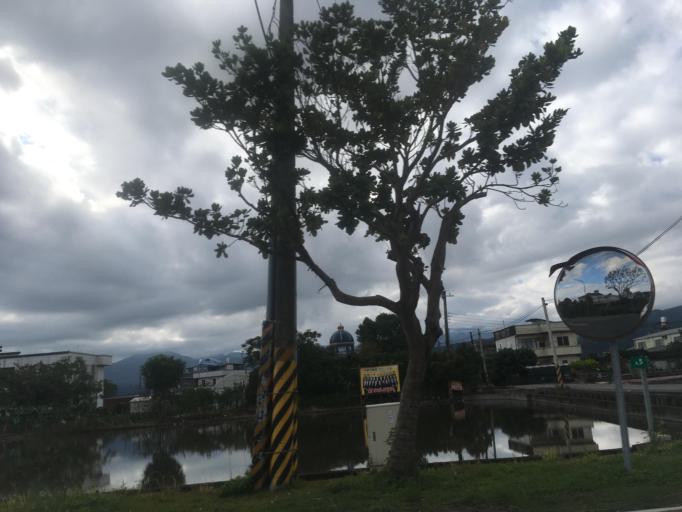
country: TW
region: Taiwan
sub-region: Yilan
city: Yilan
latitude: 24.6852
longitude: 121.7035
